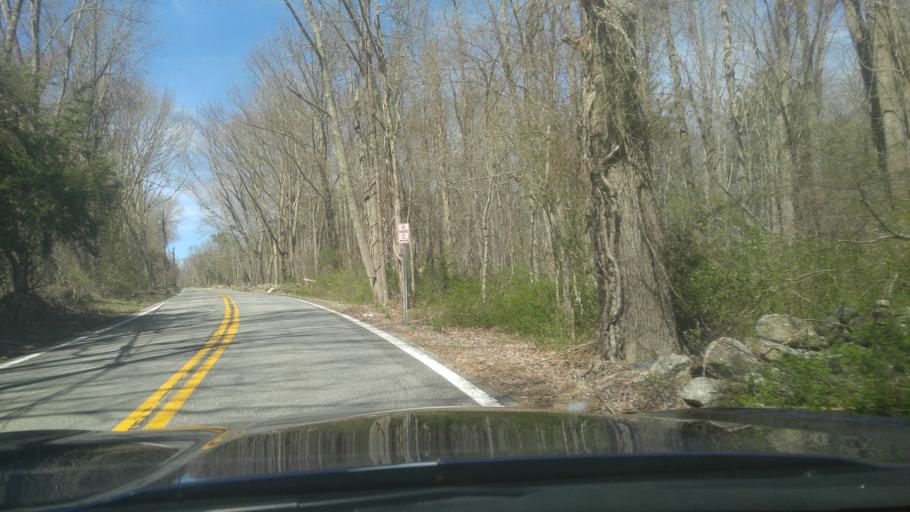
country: US
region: Rhode Island
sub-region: Washington County
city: Hope Valley
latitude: 41.5880
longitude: -71.7584
